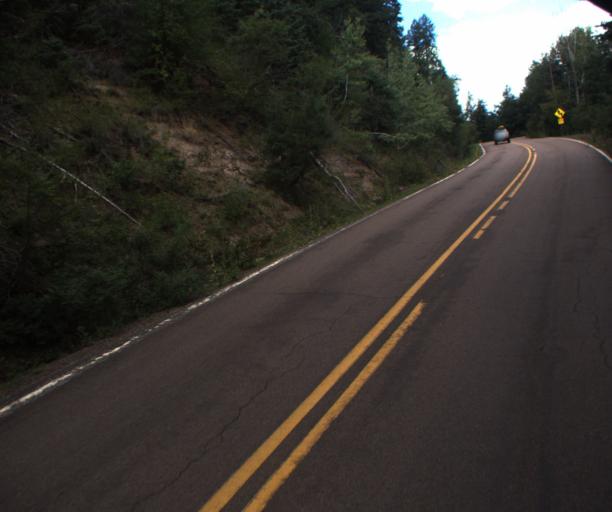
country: US
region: Arizona
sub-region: Navajo County
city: Pinetop-Lakeside
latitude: 34.0219
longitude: -109.7825
